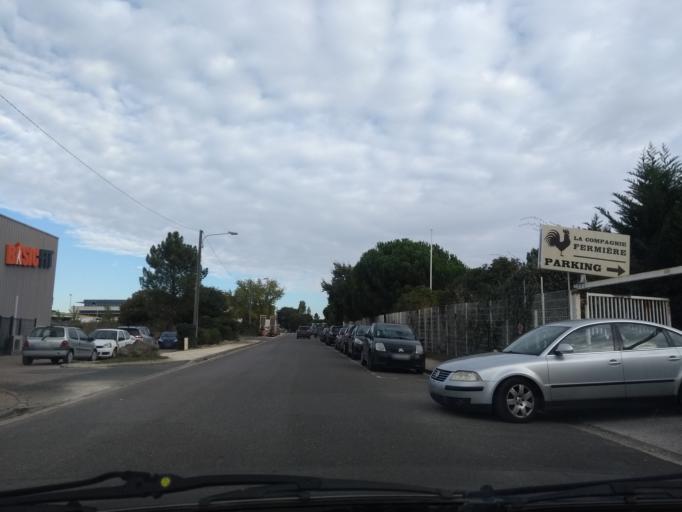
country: FR
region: Aquitaine
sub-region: Departement de la Gironde
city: Canejan
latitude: 44.7747
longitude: -0.6396
